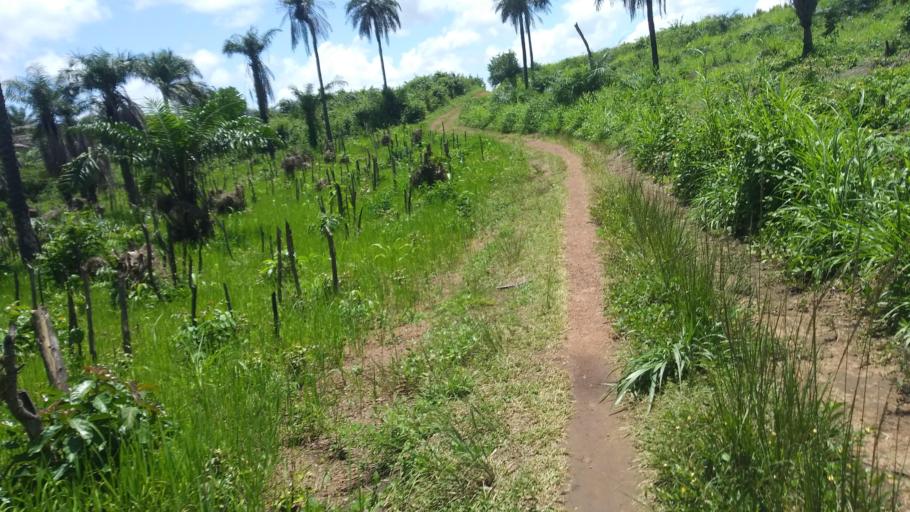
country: SL
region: Northern Province
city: Binkolo
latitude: 8.9111
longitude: -11.9781
